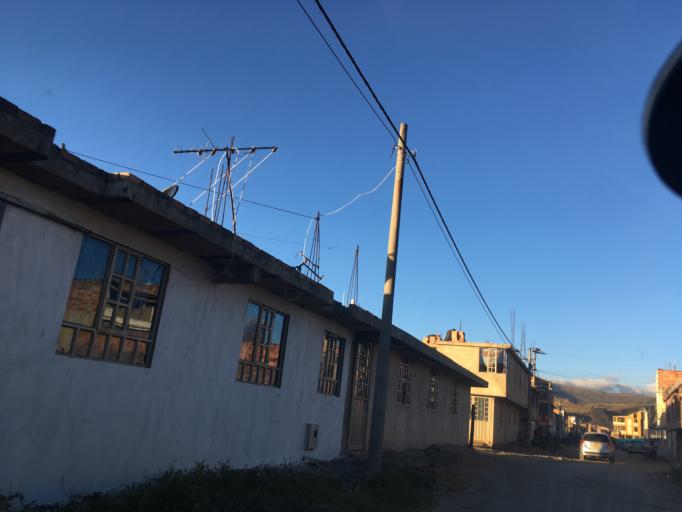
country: CO
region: Boyaca
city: Aquitania
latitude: 5.5162
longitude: -72.8871
